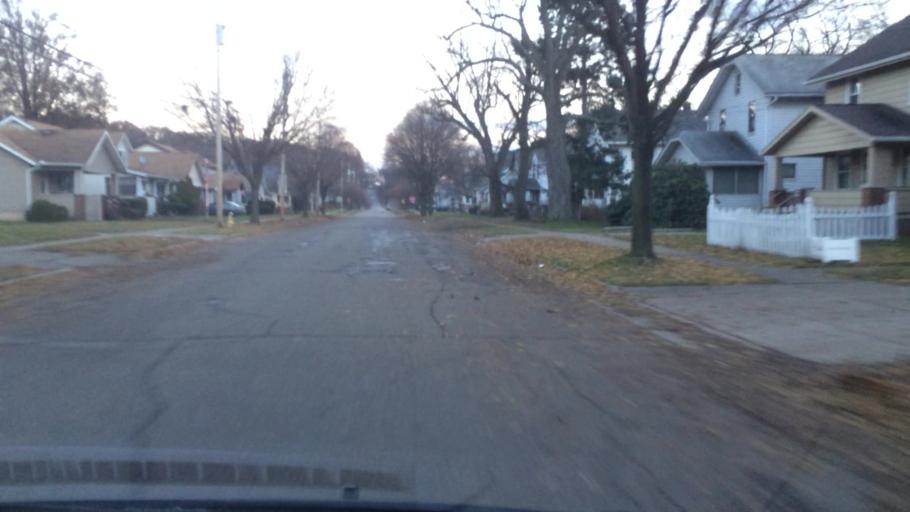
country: US
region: Ohio
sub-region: Summit County
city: Sawyerwood
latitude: 41.0652
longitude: -81.4642
